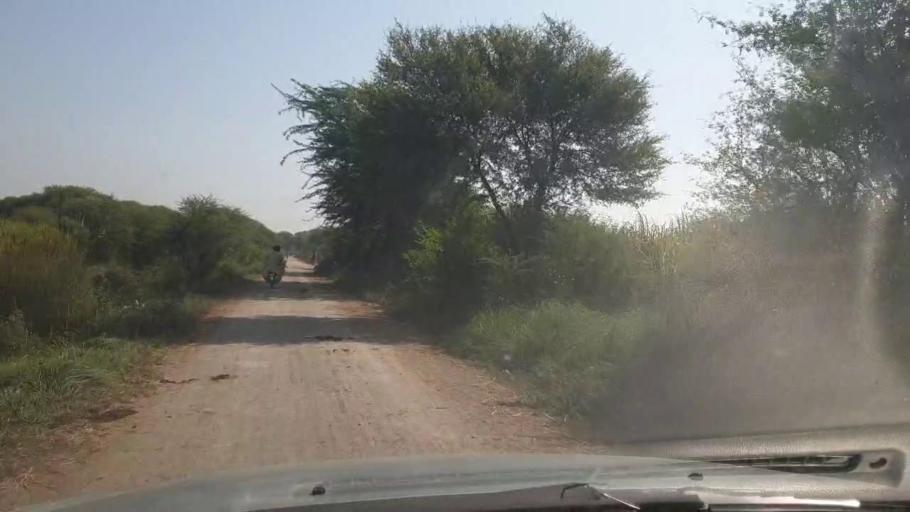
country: PK
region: Sindh
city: Bulri
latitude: 24.9119
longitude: 68.4465
